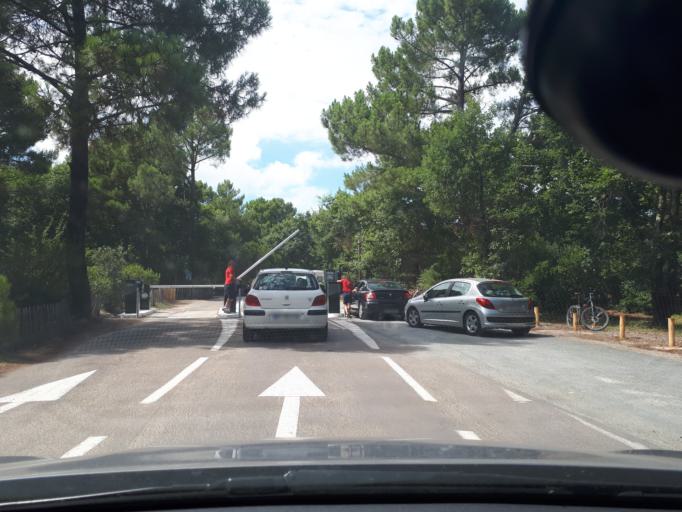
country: FR
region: Aquitaine
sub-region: Departement de la Gironde
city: Arcachon
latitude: 44.5975
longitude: -1.1971
